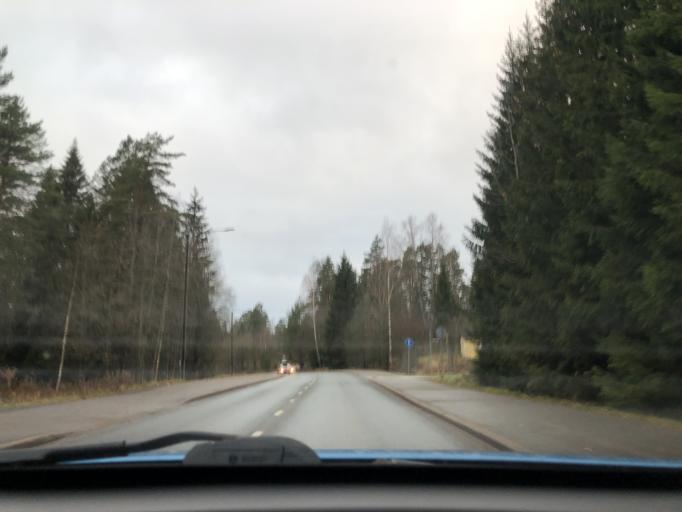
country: FI
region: Pirkanmaa
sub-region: Tampere
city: Kangasala
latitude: 61.5275
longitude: 24.0167
